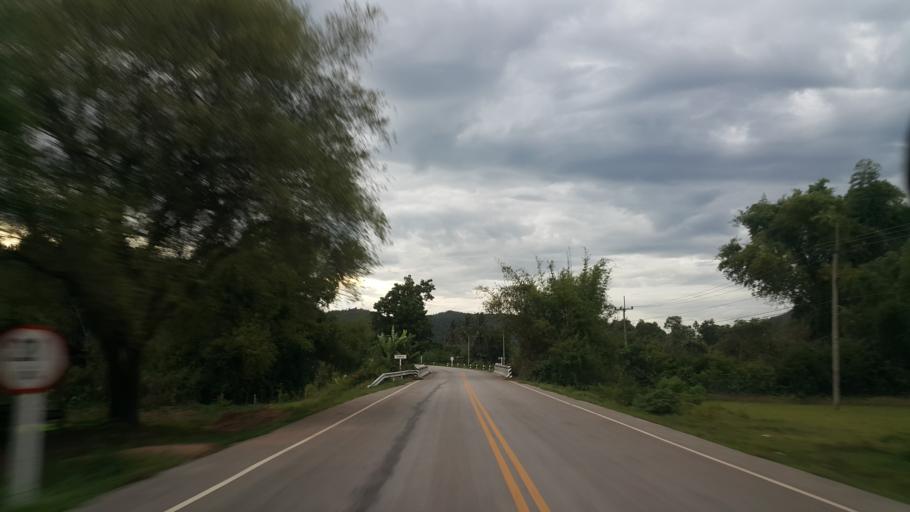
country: TH
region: Loei
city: Na Haeo
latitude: 17.5068
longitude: 101.1827
